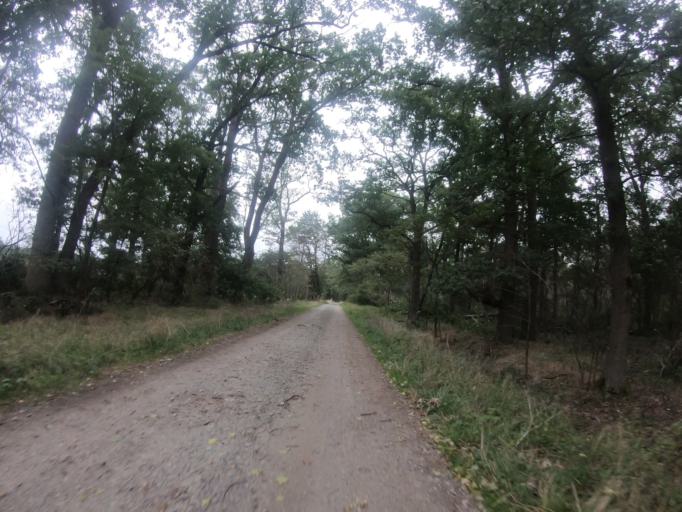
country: DE
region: Lower Saxony
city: Ribbesbuttel
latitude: 52.4497
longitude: 10.5242
